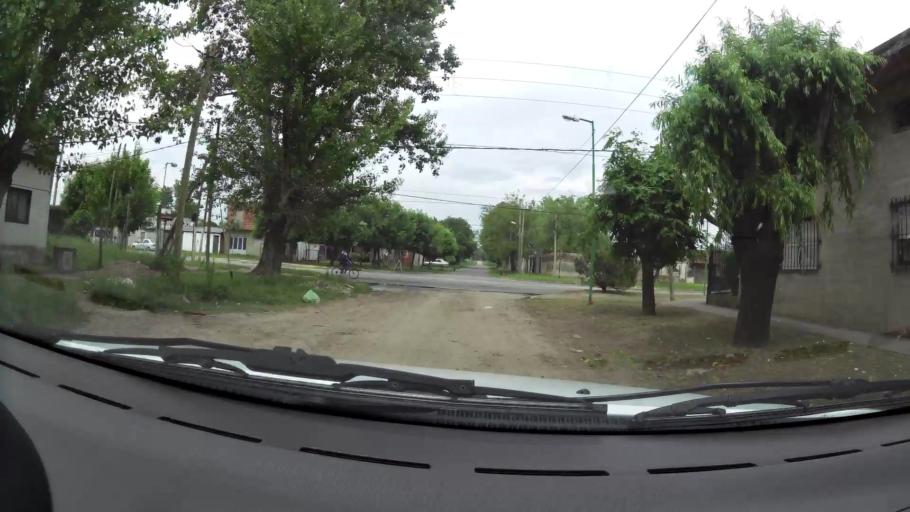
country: AR
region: Buenos Aires
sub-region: Partido de La Plata
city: La Plata
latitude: -34.9327
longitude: -58.0084
